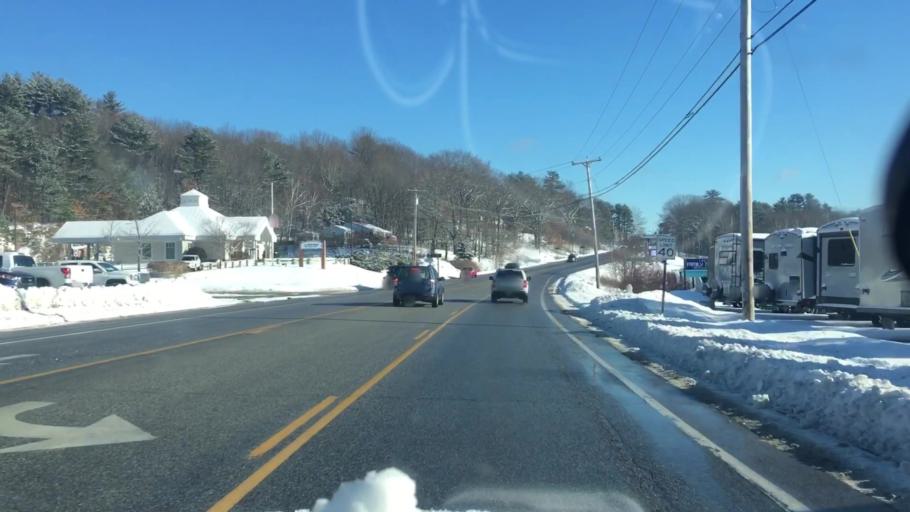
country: US
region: Maine
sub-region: Cumberland County
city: Raymond
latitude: 43.9696
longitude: -70.5932
